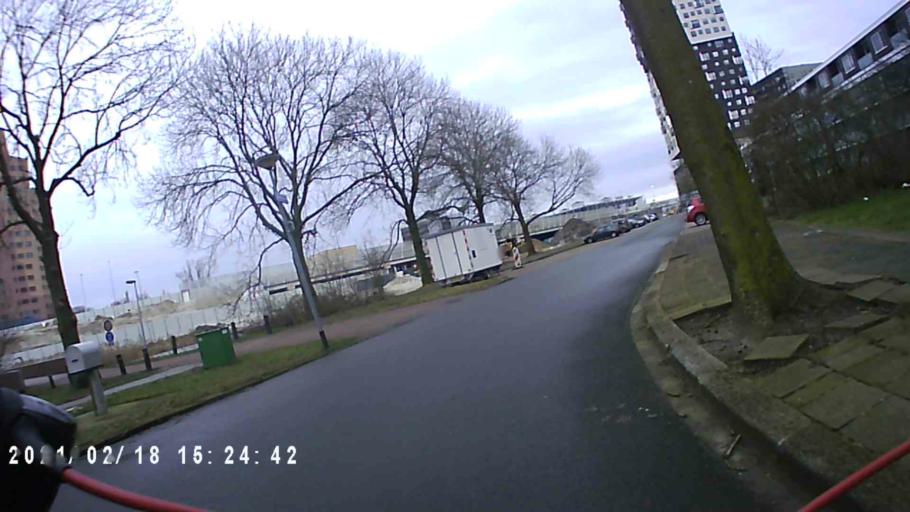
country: NL
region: Groningen
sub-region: Gemeente Groningen
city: Groningen
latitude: 53.1993
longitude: 6.5527
